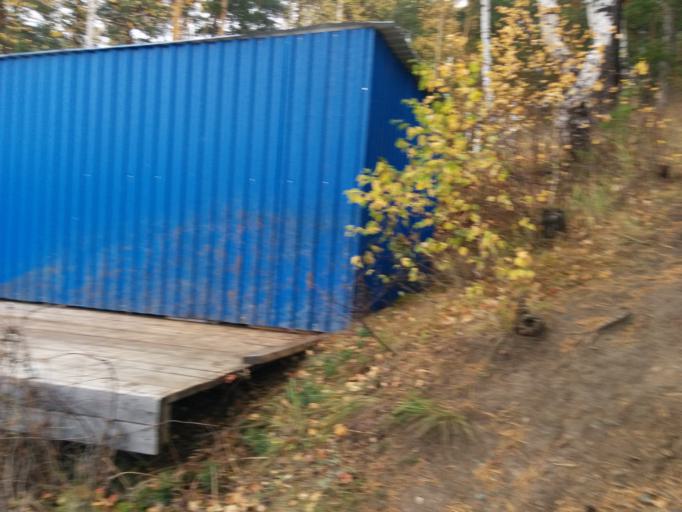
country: RU
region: Chelyabinsk
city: Turgoyak
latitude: 55.1673
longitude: 60.1074
